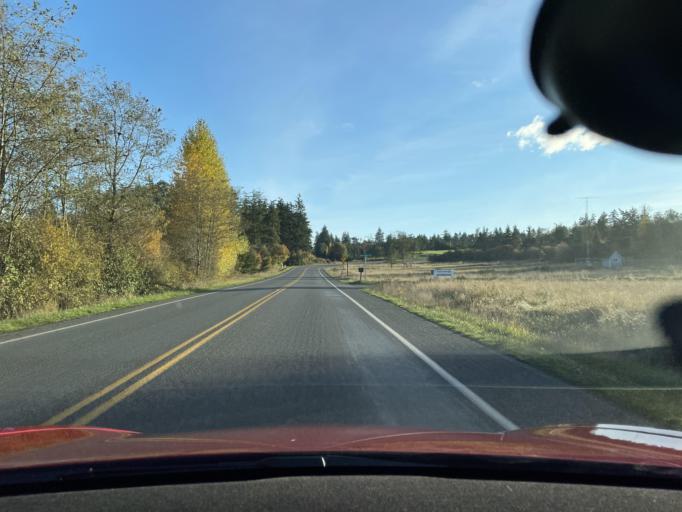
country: US
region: Washington
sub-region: San Juan County
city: Friday Harbor
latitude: 48.5131
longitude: -123.0231
